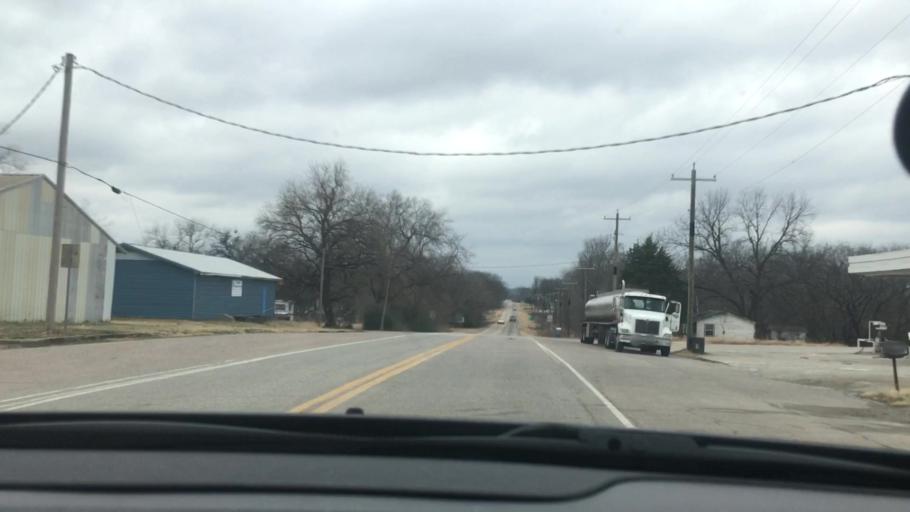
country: US
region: Oklahoma
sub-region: Coal County
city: Coalgate
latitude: 34.3750
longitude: -96.4248
